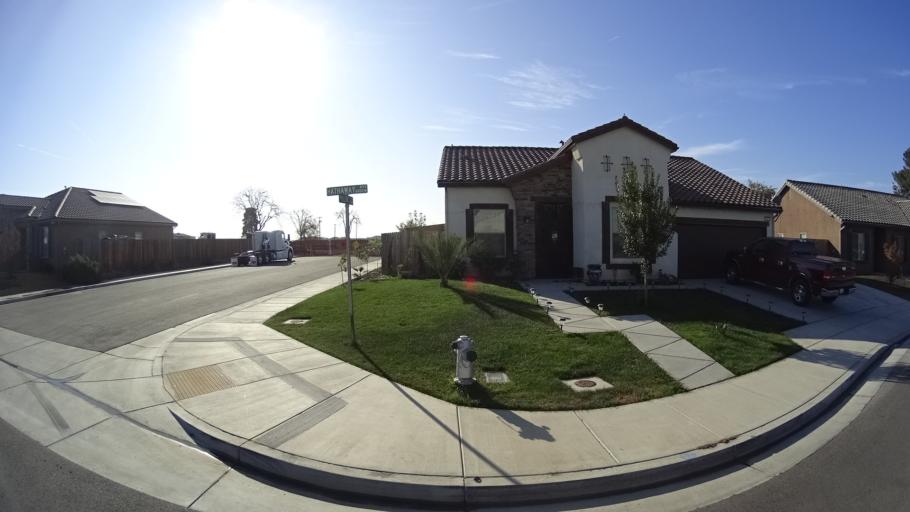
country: US
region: California
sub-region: Kern County
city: Greenfield
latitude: 35.2688
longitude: -119.0733
